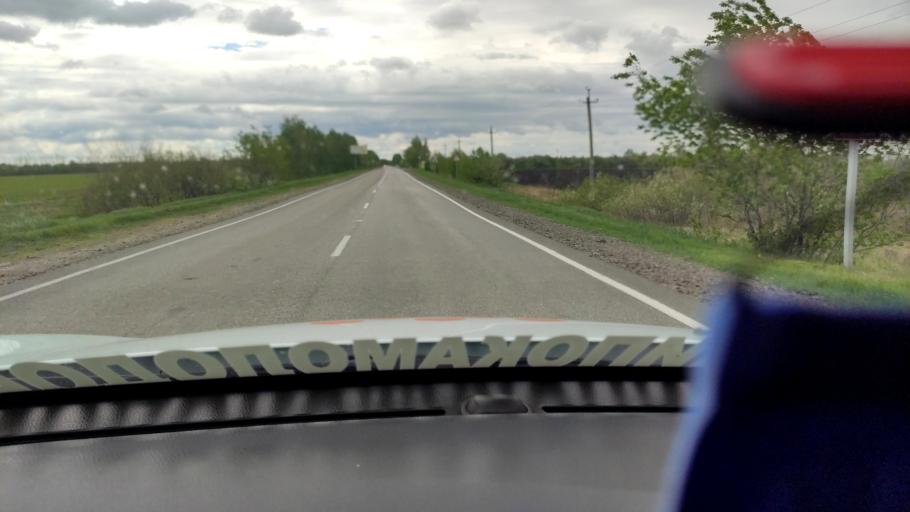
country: RU
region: Voronezj
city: Imeni Pervogo Maya
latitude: 50.7737
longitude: 39.3854
